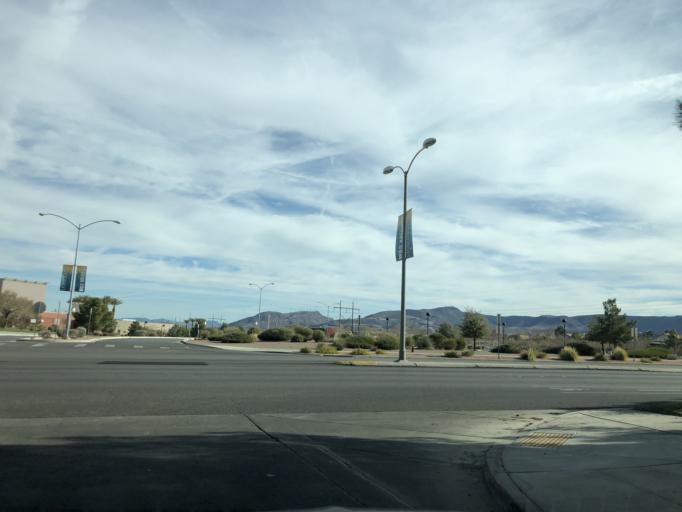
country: US
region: Nevada
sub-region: Clark County
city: Whitney
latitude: 36.0185
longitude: -115.0833
